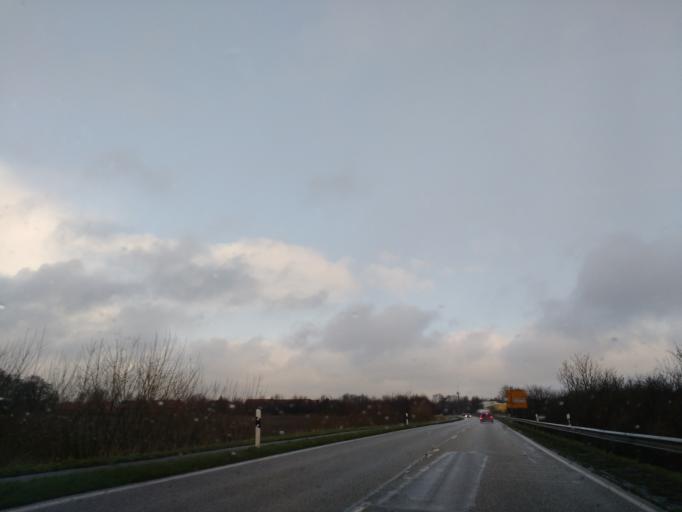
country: DE
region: Schleswig-Holstein
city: Goosefeld
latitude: 54.4438
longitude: 9.8228
